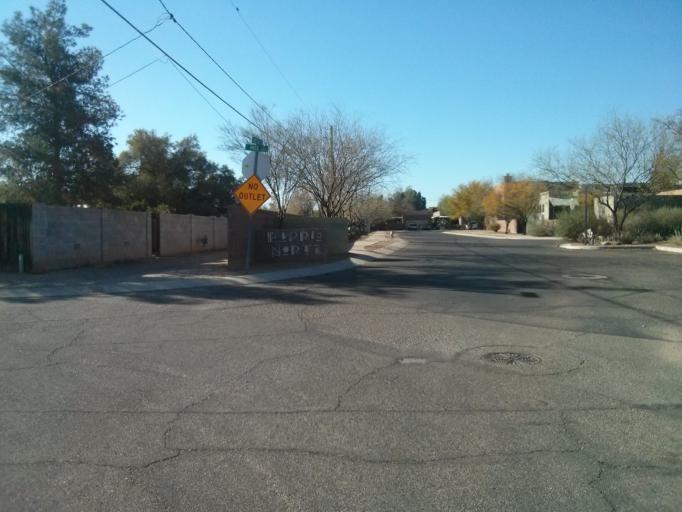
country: US
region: Arizona
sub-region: Pima County
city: Catalina Foothills
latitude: 32.2778
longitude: -110.9503
